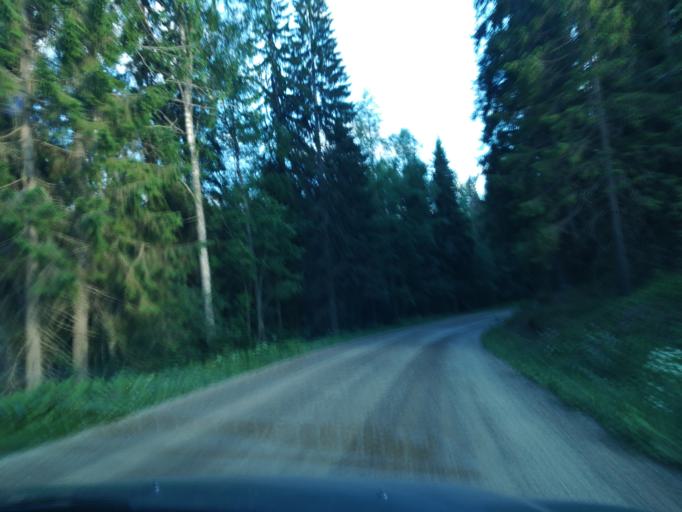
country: FI
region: Southern Savonia
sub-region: Mikkeli
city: Puumala
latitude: 61.6270
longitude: 28.1083
